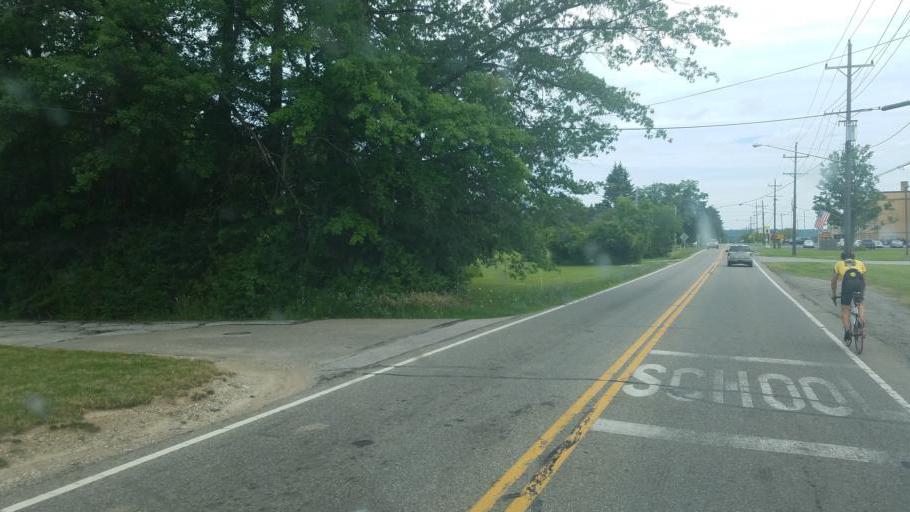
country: US
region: Ohio
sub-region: Geauga County
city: Burton
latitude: 41.4637
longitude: -81.2443
